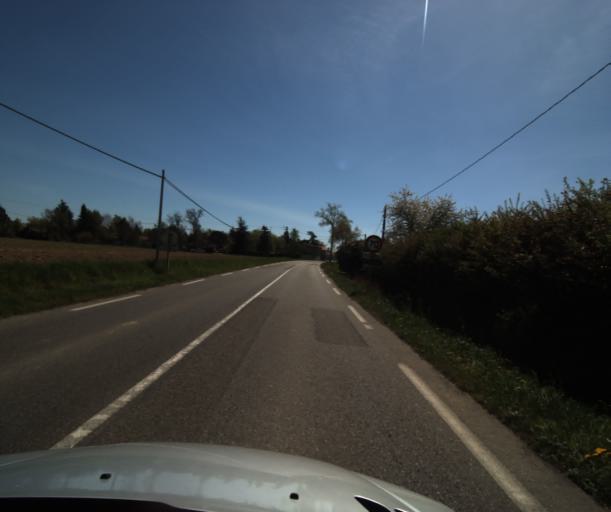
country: FR
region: Midi-Pyrenees
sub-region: Departement du Tarn-et-Garonne
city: Montbeton
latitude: 44.0487
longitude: 1.2974
